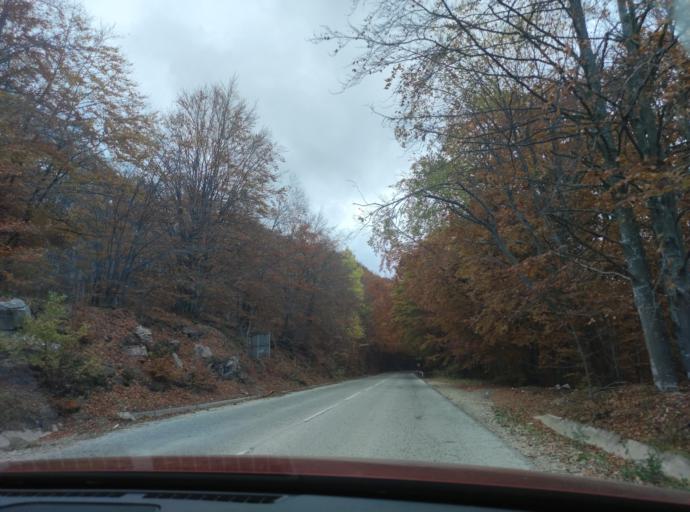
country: BG
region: Sofiya
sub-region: Obshtina Godech
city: Godech
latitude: 43.1144
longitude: 23.1111
